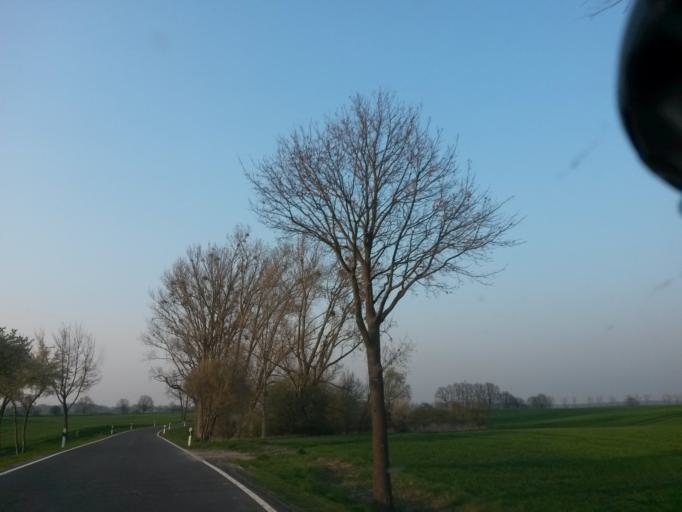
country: DE
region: Brandenburg
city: Buckow
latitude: 52.6319
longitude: 14.0697
